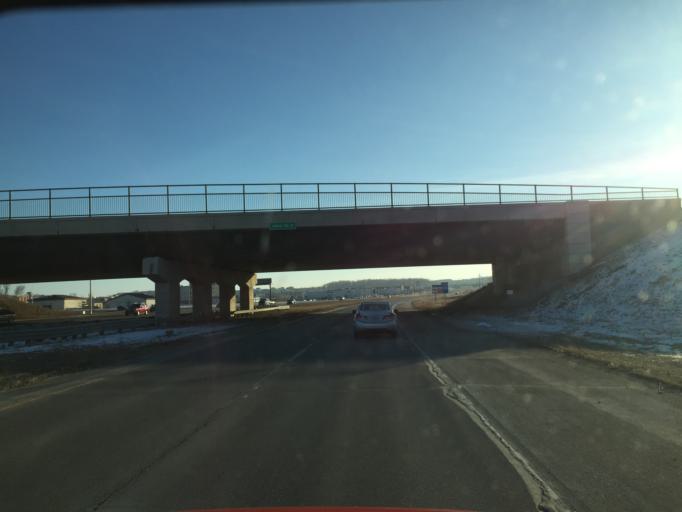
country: US
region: Minnesota
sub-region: Olmsted County
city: Rochester
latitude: 43.9645
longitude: -92.4636
